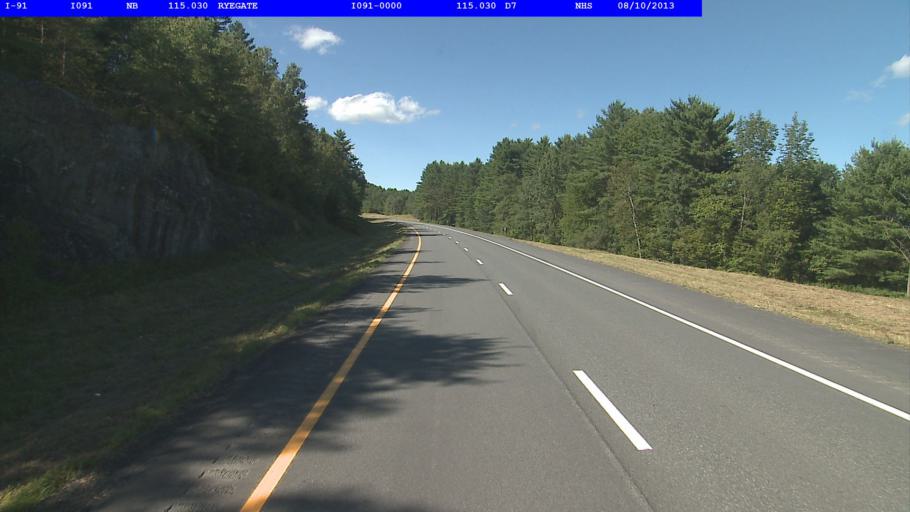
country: US
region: New Hampshire
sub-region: Grafton County
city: Woodsville
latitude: 44.2253
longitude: -72.0669
